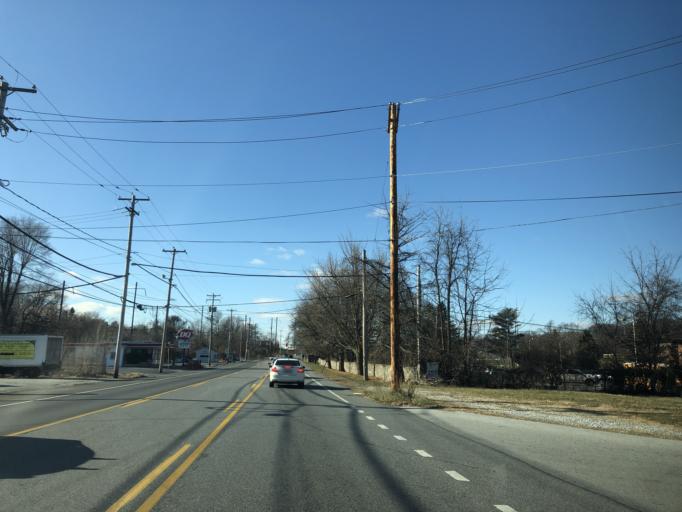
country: US
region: Pennsylvania
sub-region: Chester County
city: Caln
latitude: 39.9887
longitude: -75.7903
